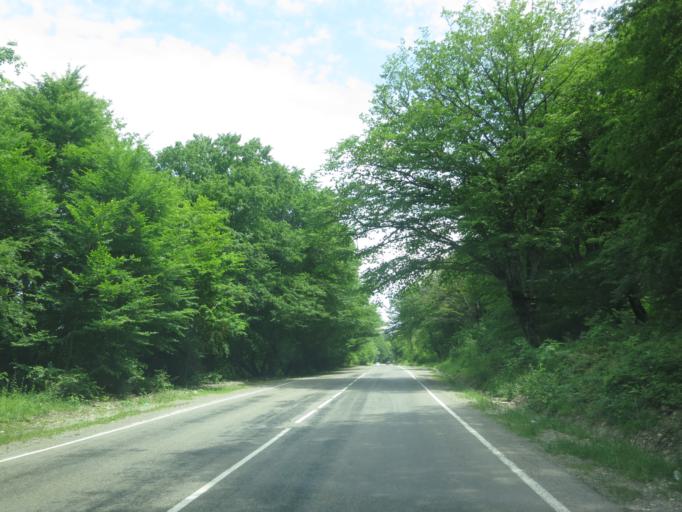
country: GE
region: Kakheti
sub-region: Telavi
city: Telavi
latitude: 41.9069
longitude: 45.3773
